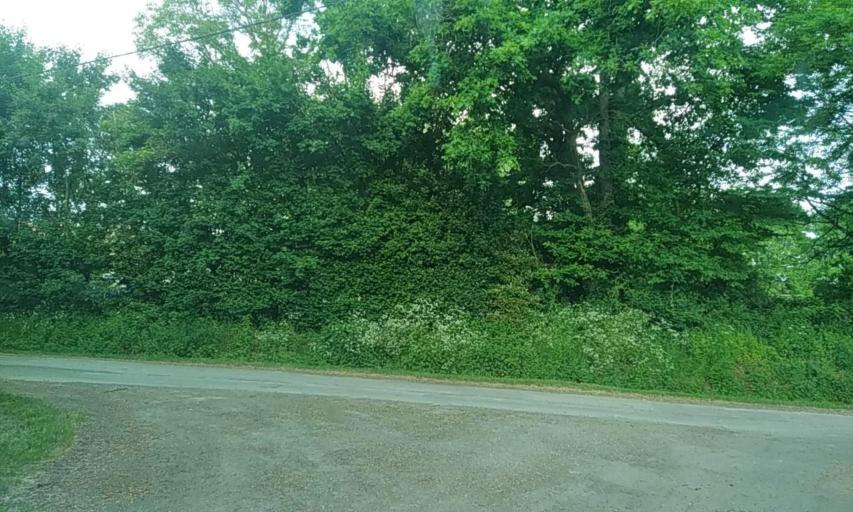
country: FR
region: Poitou-Charentes
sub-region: Departement des Deux-Sevres
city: Boisme
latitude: 46.7604
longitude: -0.4414
